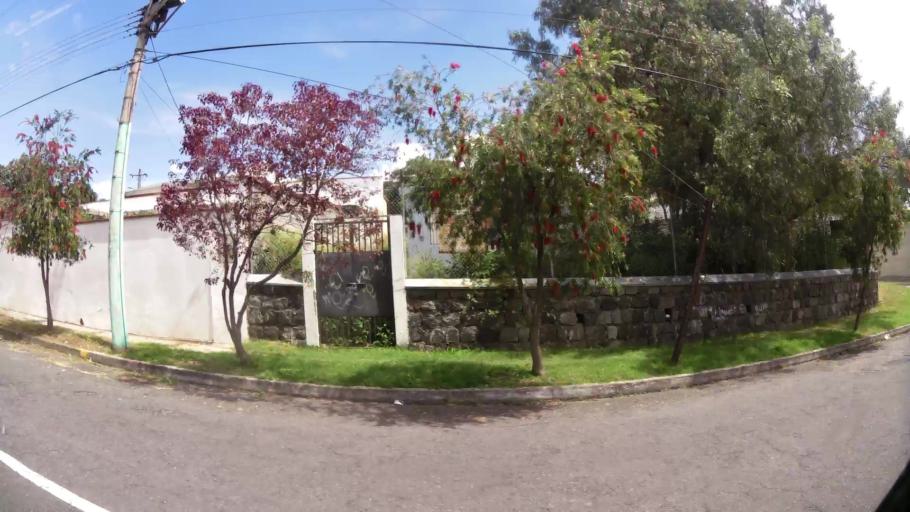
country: EC
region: Pichincha
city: Quito
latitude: -0.2114
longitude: -78.4289
